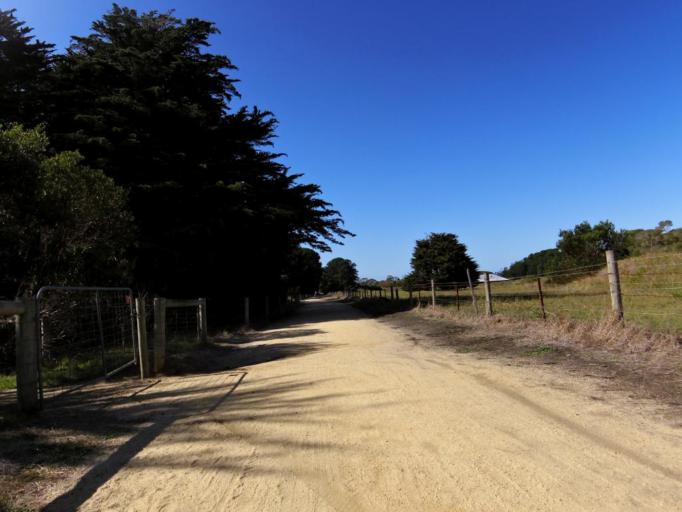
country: AU
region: Victoria
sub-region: Bass Coast
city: North Wonthaggi
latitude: -38.6006
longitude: 145.5728
